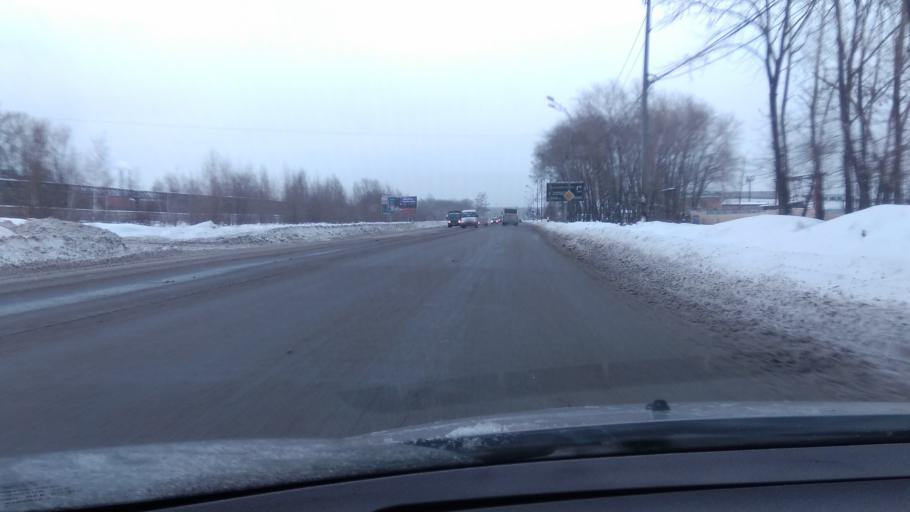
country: RU
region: Sverdlovsk
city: Nizhniy Tagil
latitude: 57.9090
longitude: 60.0110
